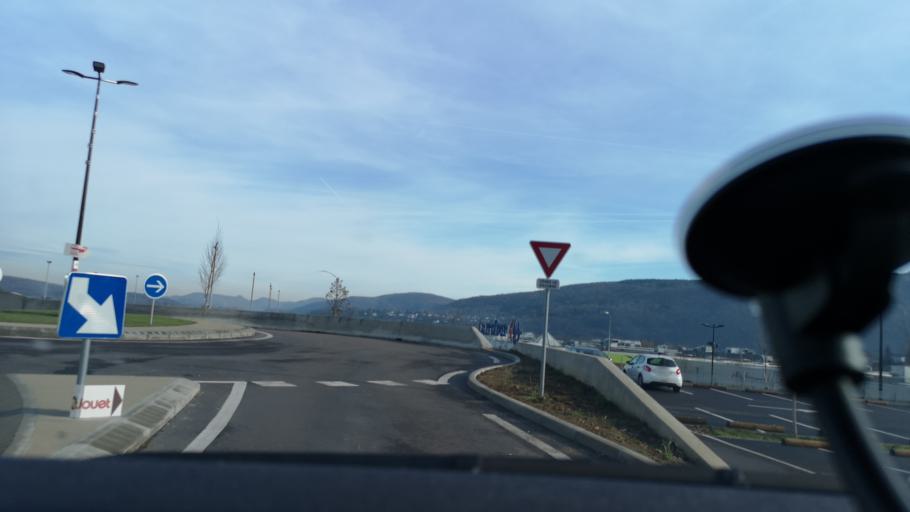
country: FR
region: Franche-Comte
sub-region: Departement du Doubs
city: Thise
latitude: 47.2621
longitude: 6.0621
